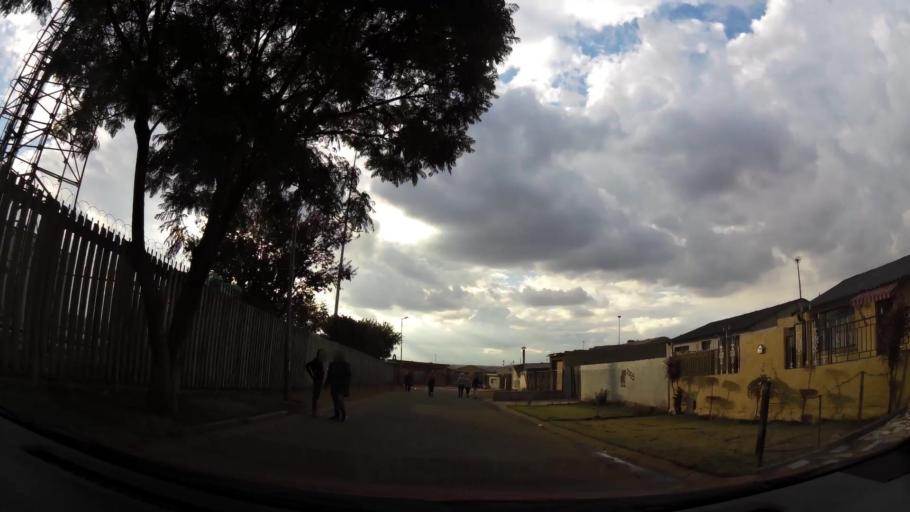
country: ZA
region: Gauteng
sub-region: City of Johannesburg Metropolitan Municipality
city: Soweto
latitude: -26.2387
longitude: 27.8241
